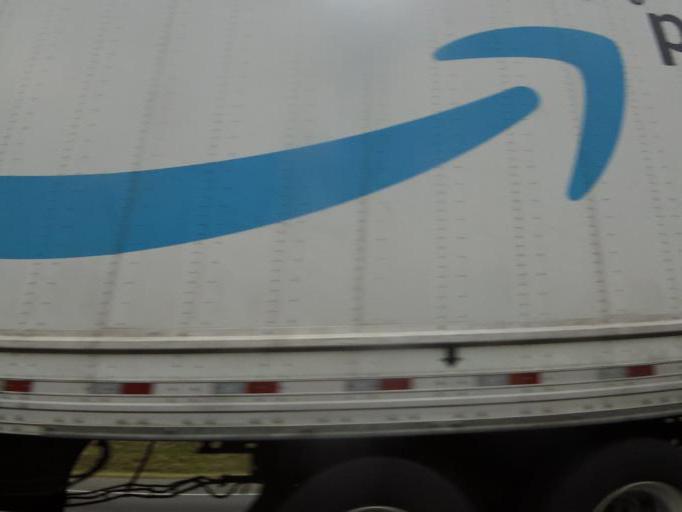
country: US
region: Alabama
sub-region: Jefferson County
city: Gardendale
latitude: 33.6313
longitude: -86.8229
